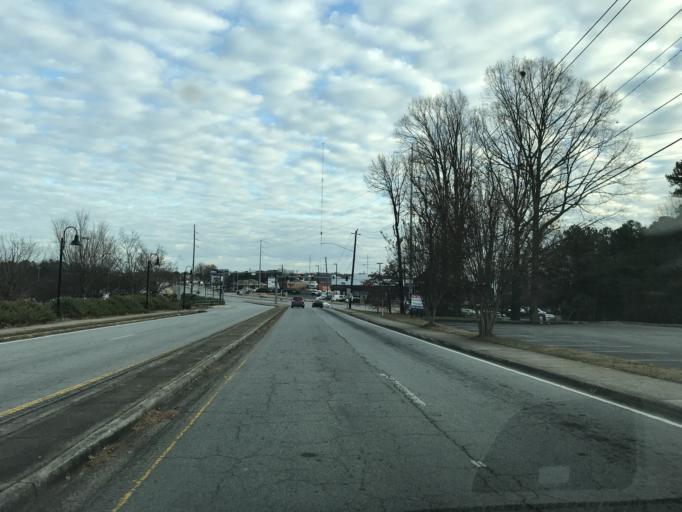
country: US
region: Georgia
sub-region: DeKalb County
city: Tucker
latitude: 33.8501
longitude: -84.2579
